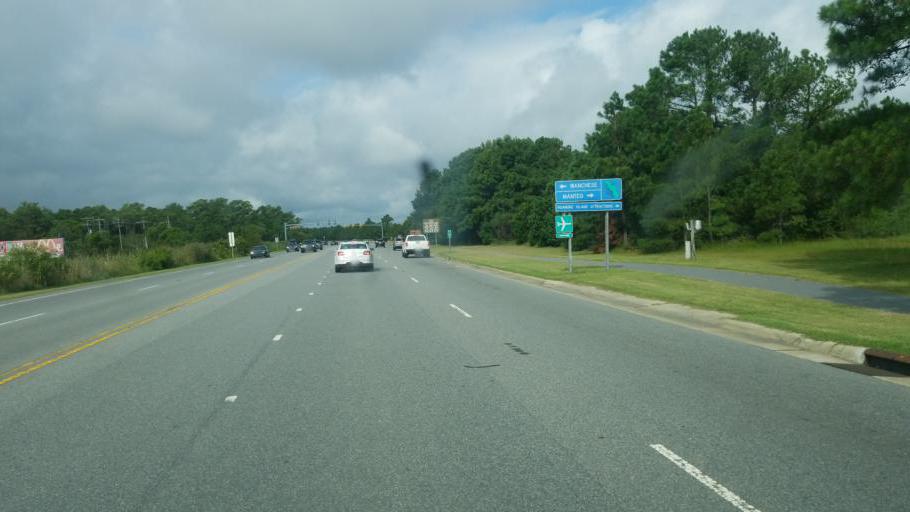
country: US
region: North Carolina
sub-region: Dare County
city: Manteo
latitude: 35.8903
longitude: -75.6582
